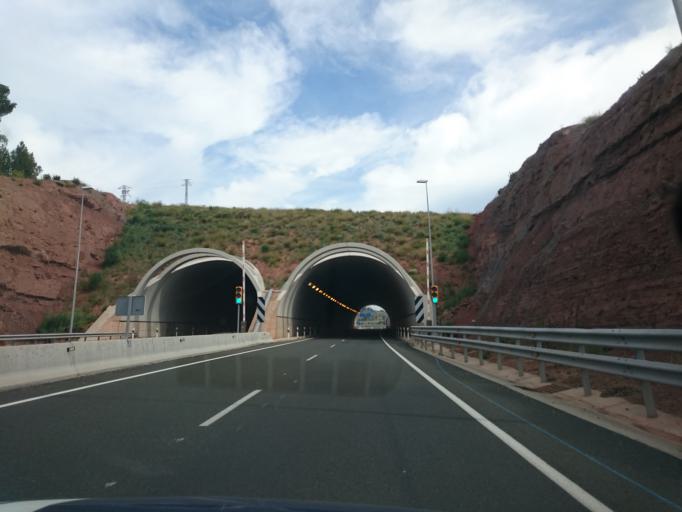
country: ES
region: Catalonia
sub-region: Provincia de Barcelona
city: Sant Joan de Vilatorrada
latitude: 41.7275
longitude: 1.7819
